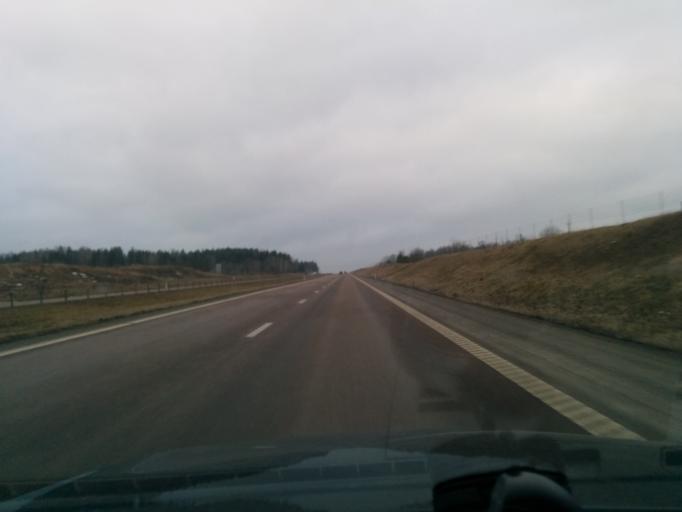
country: SE
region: Uppsala
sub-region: Enkopings Kommun
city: Enkoping
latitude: 59.6473
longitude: 17.0108
